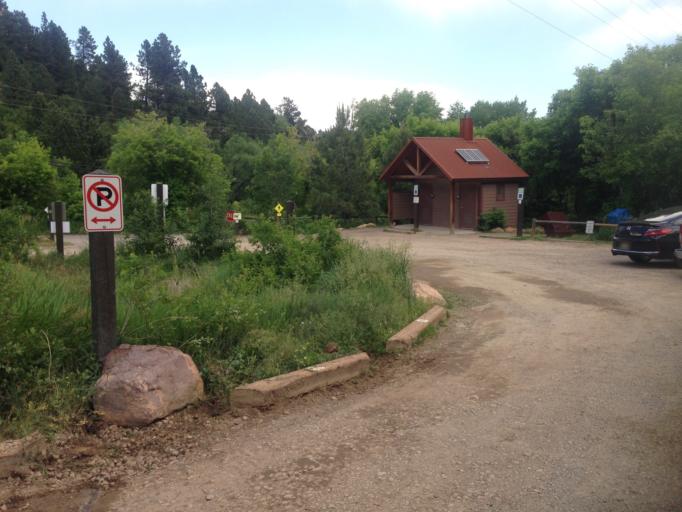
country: US
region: Colorado
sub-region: Boulder County
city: Boulder
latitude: 40.0199
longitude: -105.2978
